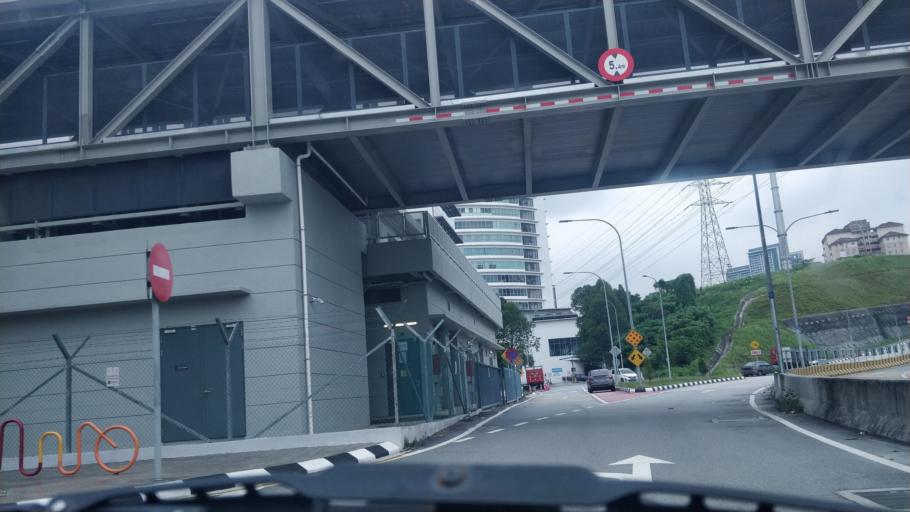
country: MY
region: Selangor
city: Kuang
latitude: 3.1975
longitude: 101.6079
